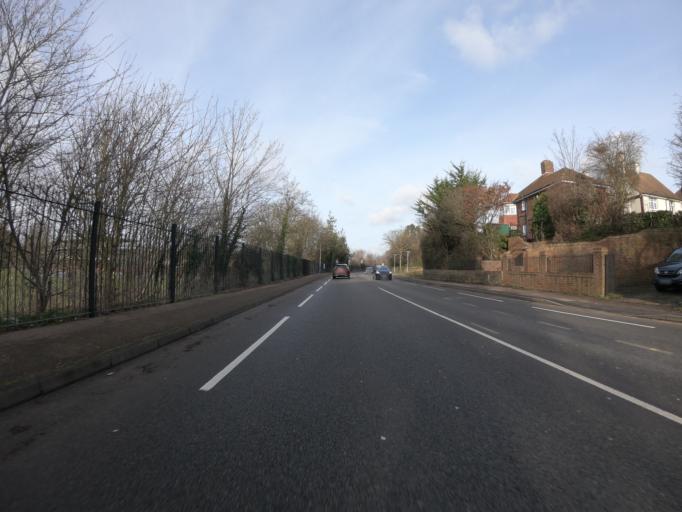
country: GB
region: England
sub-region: Kent
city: Gravesend
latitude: 51.4267
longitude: 0.3634
